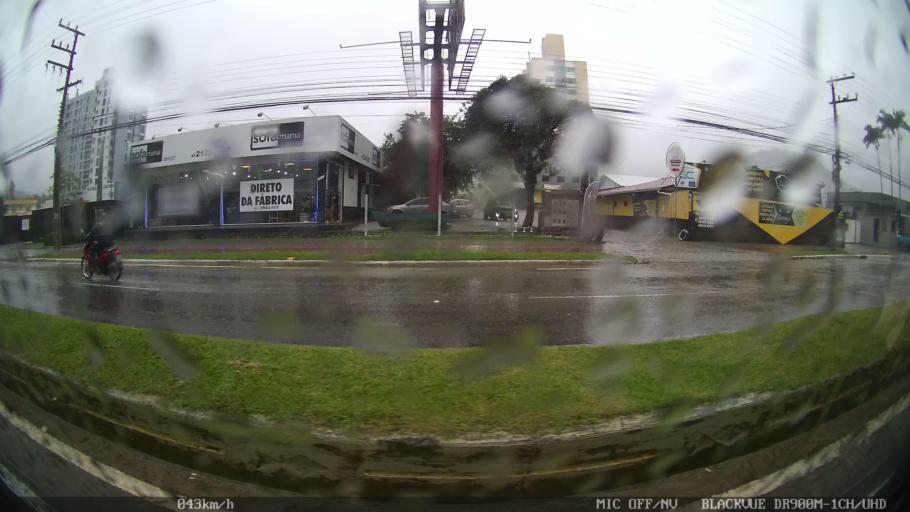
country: BR
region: Santa Catarina
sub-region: Balneario Camboriu
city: Balneario Camboriu
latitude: -26.9532
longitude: -48.6404
